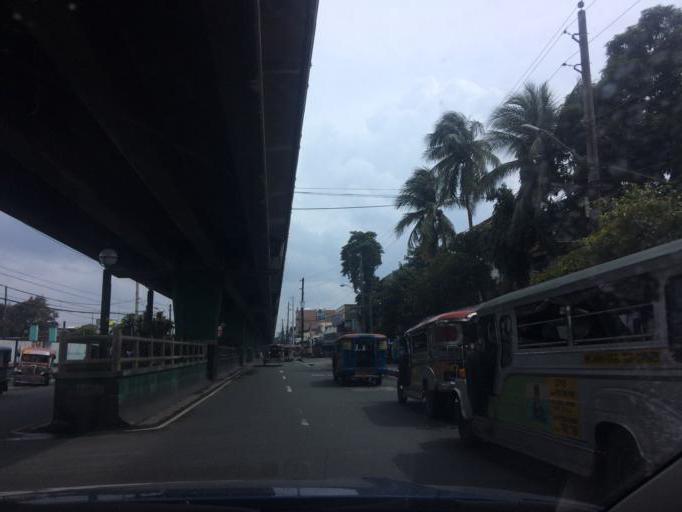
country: PH
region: Metro Manila
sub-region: Makati City
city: Makati City
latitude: 14.5532
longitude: 120.9974
